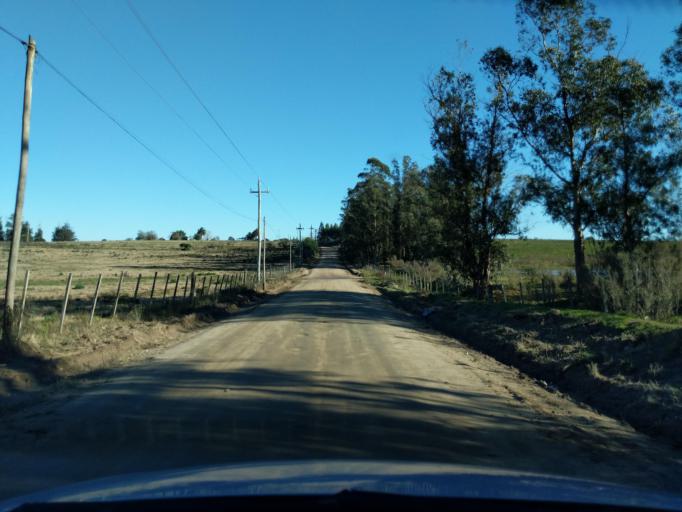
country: UY
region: Florida
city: Florida
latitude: -34.0946
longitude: -56.2427
